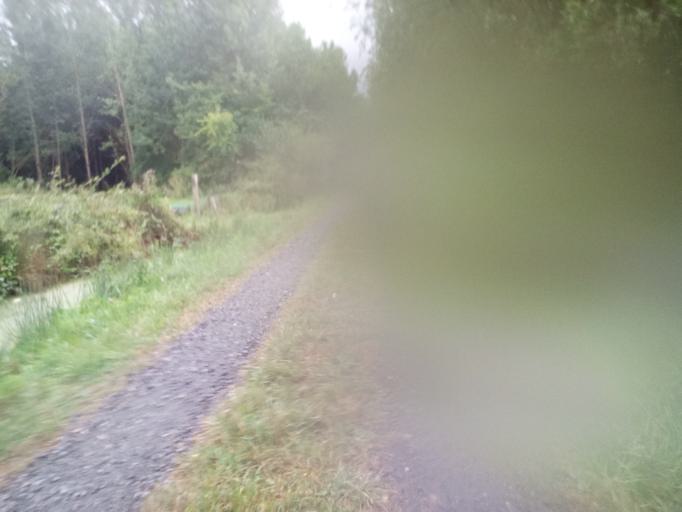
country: FR
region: Lower Normandy
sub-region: Departement du Calvados
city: Bavent
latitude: 49.2339
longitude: -0.1613
